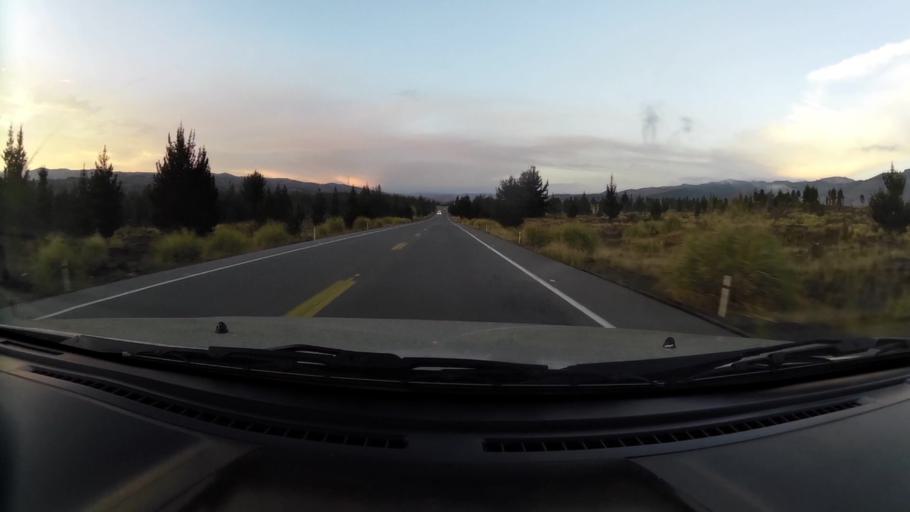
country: EC
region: Chimborazo
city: Alausi
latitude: -2.0355
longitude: -78.7363
